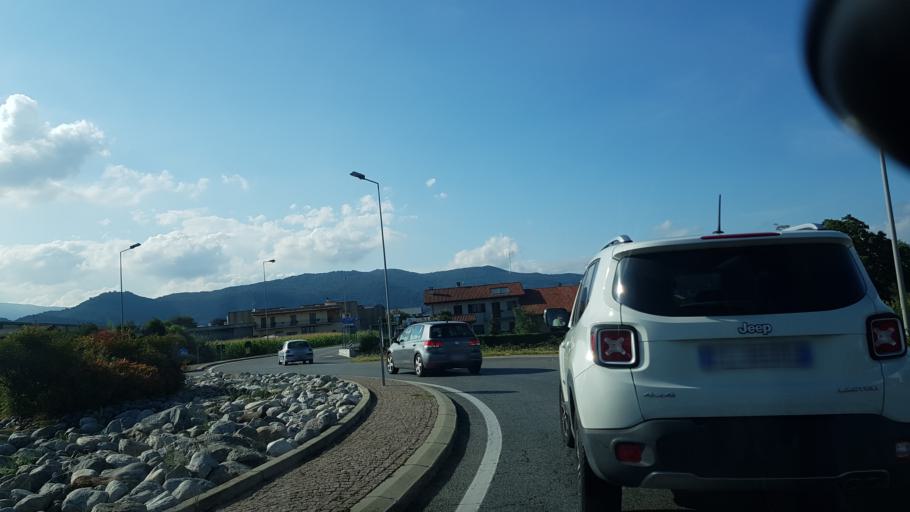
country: IT
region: Piedmont
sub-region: Provincia di Cuneo
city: Busca
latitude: 44.4992
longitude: 7.4926
